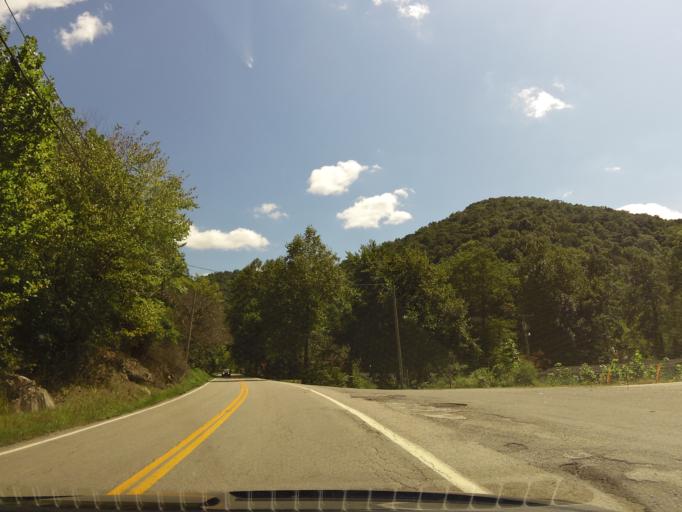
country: US
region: Kentucky
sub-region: Harlan County
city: Loyall
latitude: 36.9242
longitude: -83.3677
